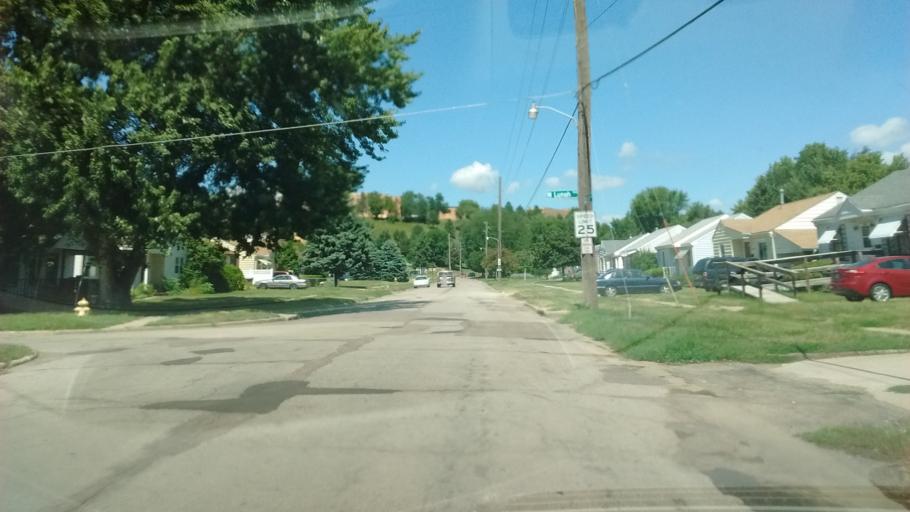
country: US
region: Iowa
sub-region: Woodbury County
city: Sioux City
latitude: 42.5224
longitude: -96.4256
